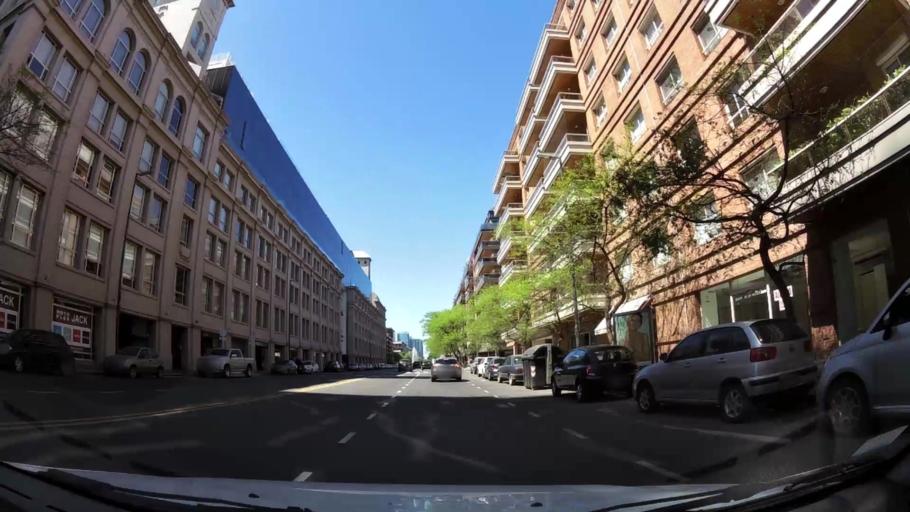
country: AR
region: Buenos Aires F.D.
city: Buenos Aires
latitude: -34.6099
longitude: -58.3627
